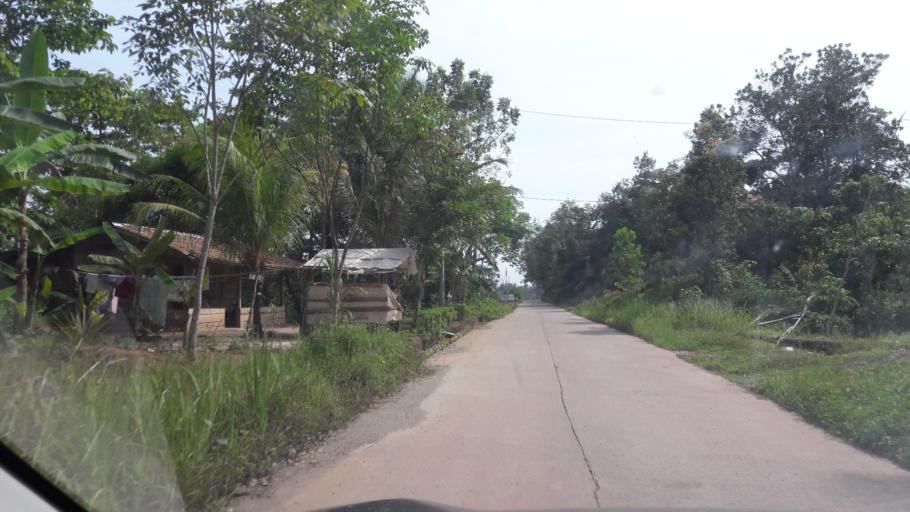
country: ID
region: South Sumatra
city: Gunungmenang
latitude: -3.3176
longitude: 104.1141
